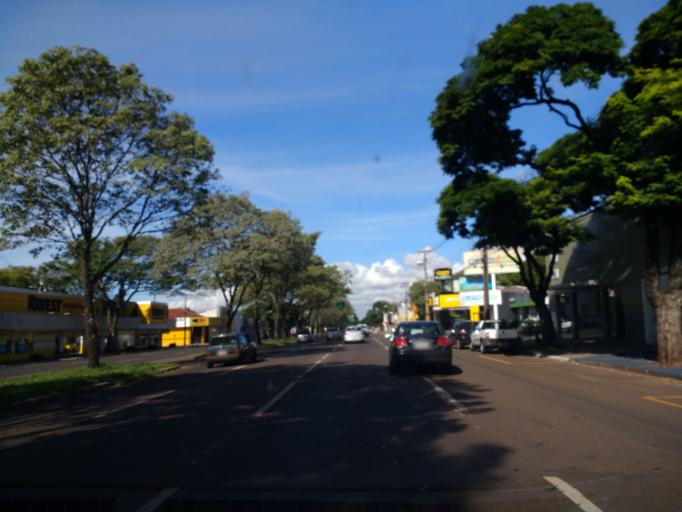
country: BR
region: Parana
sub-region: Maringa
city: Maringa
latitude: -23.4134
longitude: -51.9303
